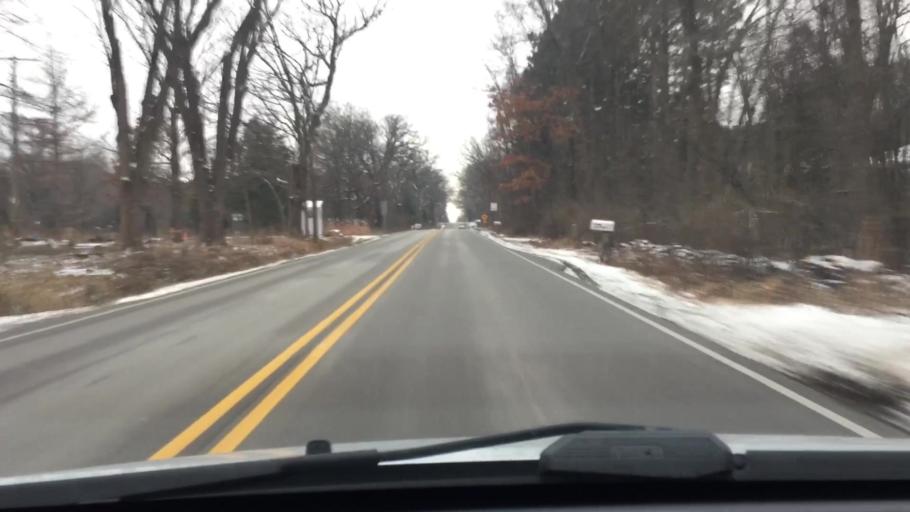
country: US
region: Wisconsin
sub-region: Waukesha County
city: Delafield
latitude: 43.0317
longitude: -88.4042
